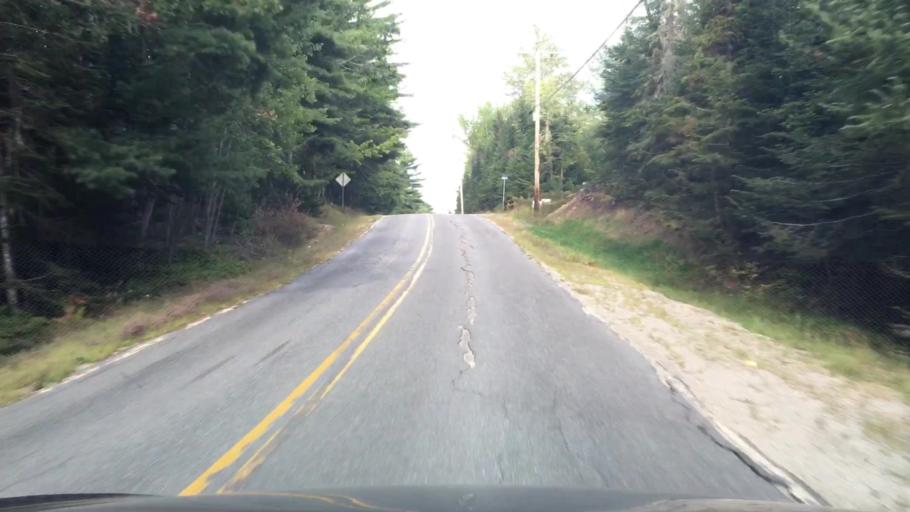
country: US
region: Maine
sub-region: Hancock County
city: Surry
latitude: 44.4935
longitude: -68.5129
